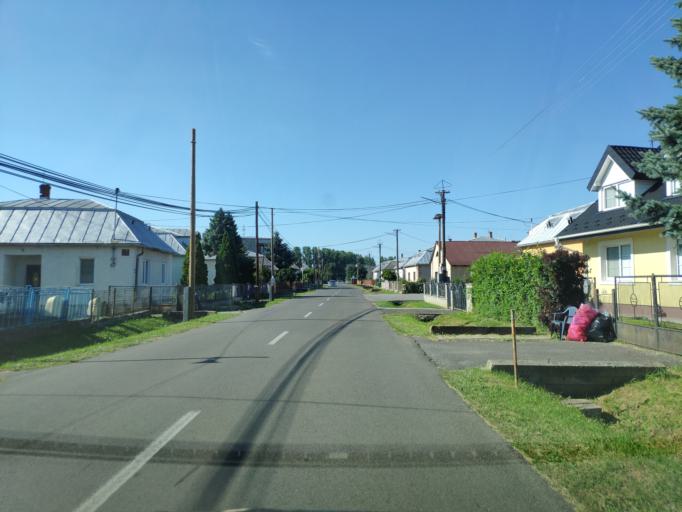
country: SK
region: Kosicky
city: Trebisov
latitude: 48.6105
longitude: 21.8464
